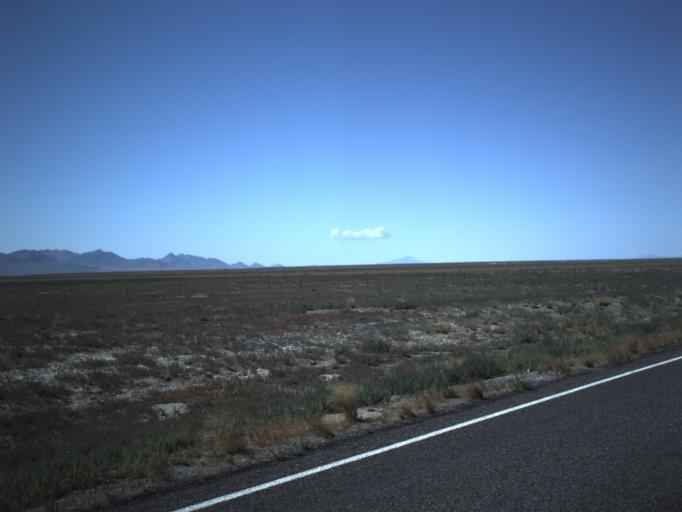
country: US
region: Utah
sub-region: Millard County
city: Delta
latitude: 39.2099
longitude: -112.9670
